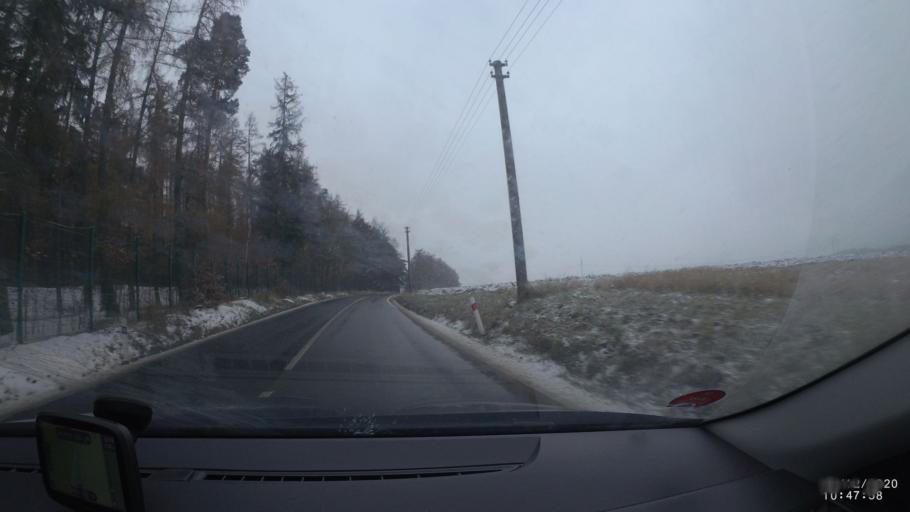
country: CZ
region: Central Bohemia
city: Nove Straseci
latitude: 50.1715
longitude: 13.8988
